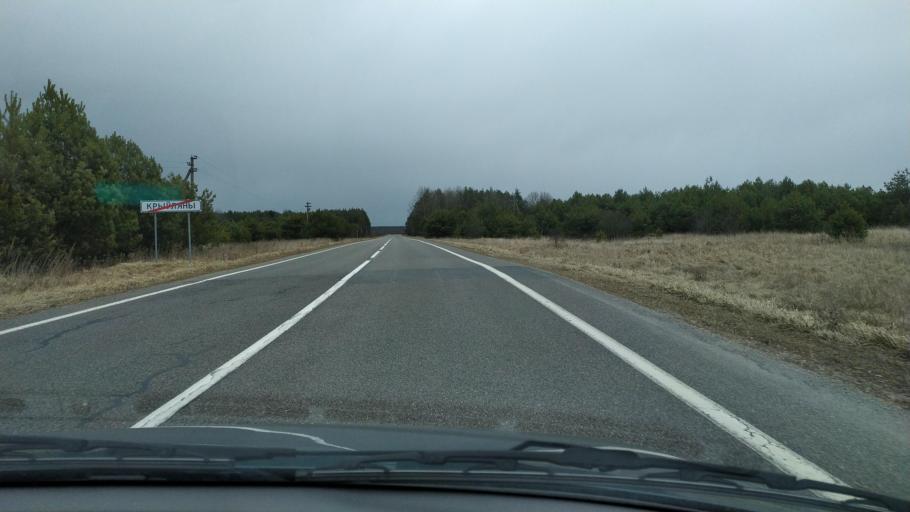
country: BY
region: Brest
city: Kamyanyets
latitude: 52.3946
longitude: 23.9854
